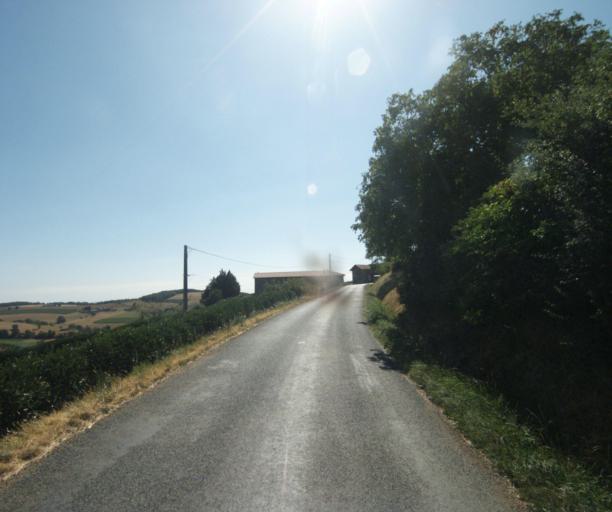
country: FR
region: Rhone-Alpes
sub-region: Departement du Rhone
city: Saint-Romain-de-Popey
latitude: 45.8241
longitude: 4.5343
